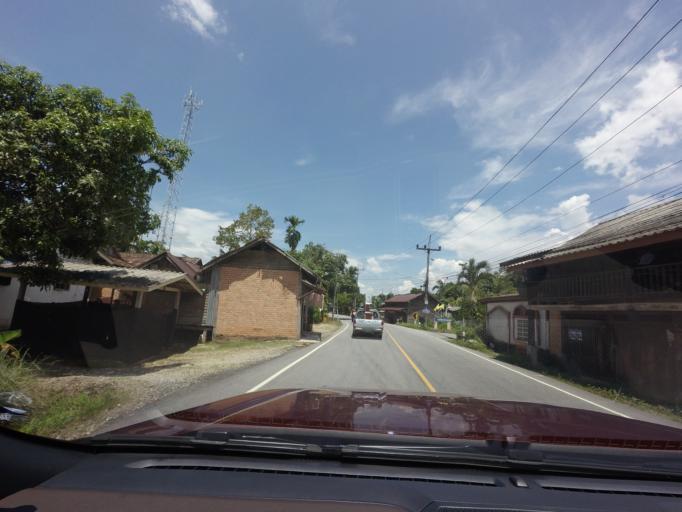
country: TH
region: Narathiwat
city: Chanae
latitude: 6.1431
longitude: 101.7020
